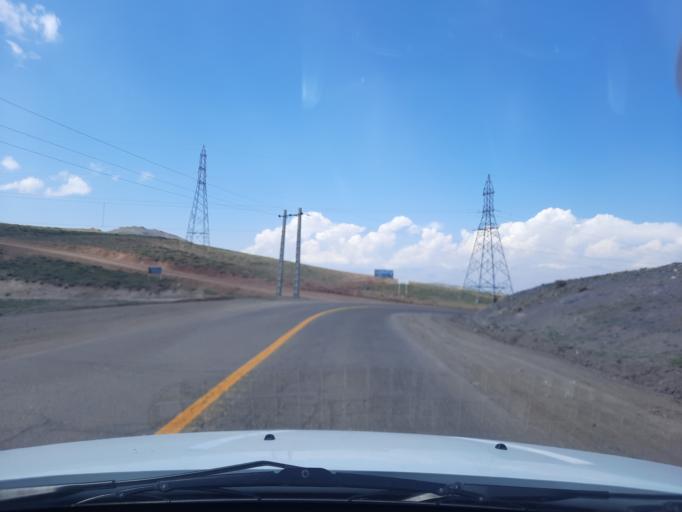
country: IR
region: Qazvin
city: Qazvin
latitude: 36.3927
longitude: 50.2073
